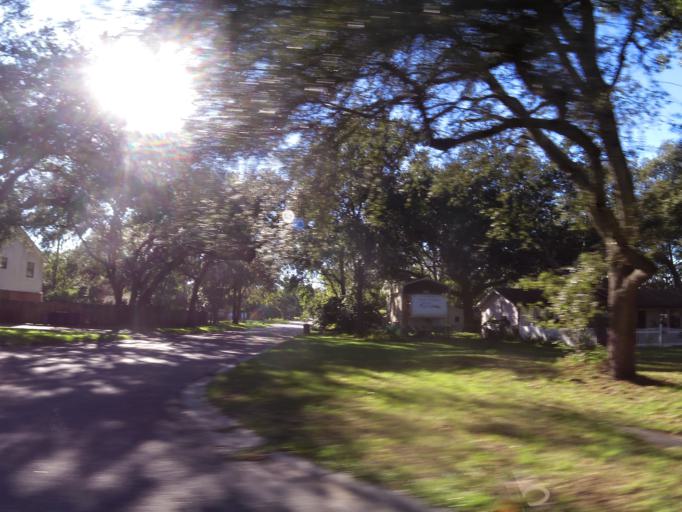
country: US
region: Florida
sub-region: Duval County
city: Atlantic Beach
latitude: 30.3270
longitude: -81.4521
